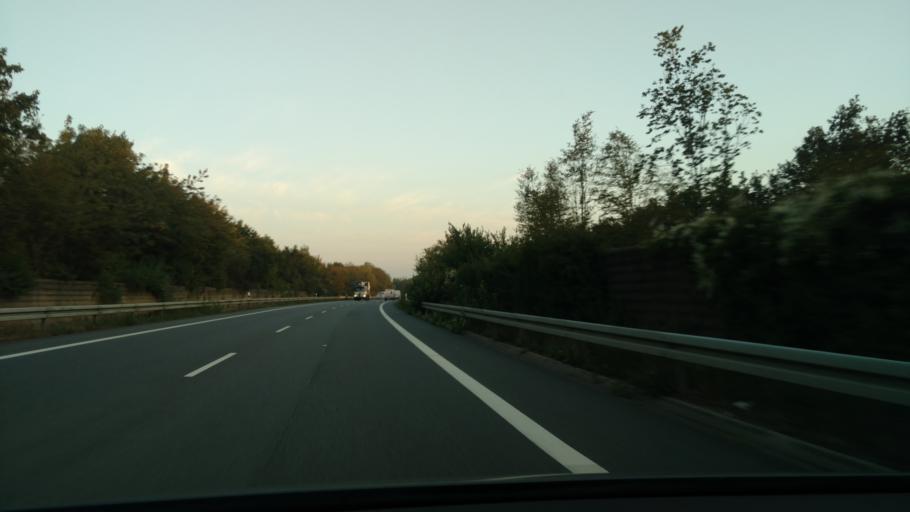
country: DE
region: North Rhine-Westphalia
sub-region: Regierungsbezirk Munster
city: Borken
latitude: 51.8374
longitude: 6.8382
